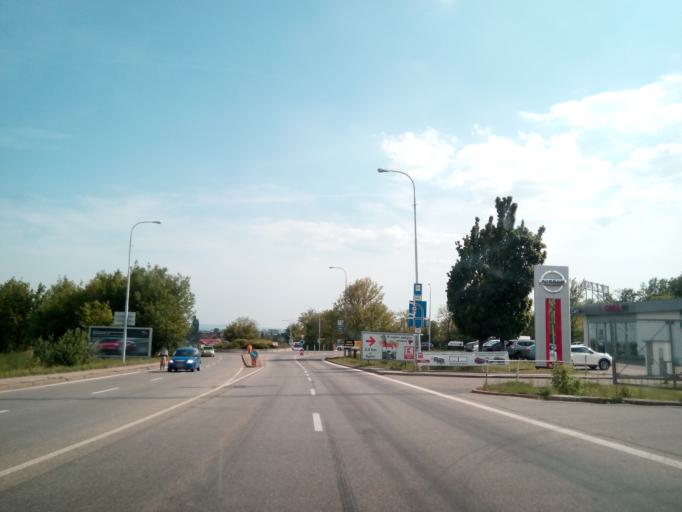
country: CZ
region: South Moravian
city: Podoli
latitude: 49.1833
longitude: 16.6918
